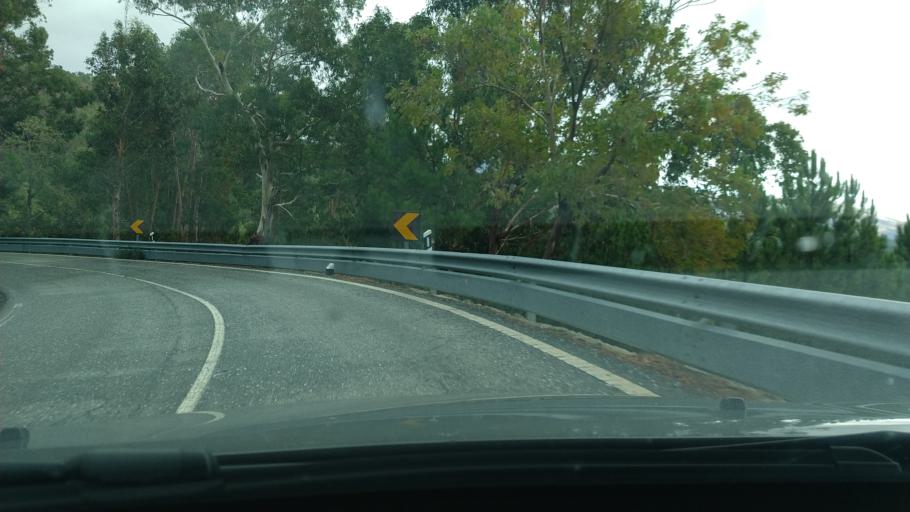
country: PT
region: Castelo Branco
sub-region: Covilha
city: Covilha
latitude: 40.2339
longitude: -7.6673
